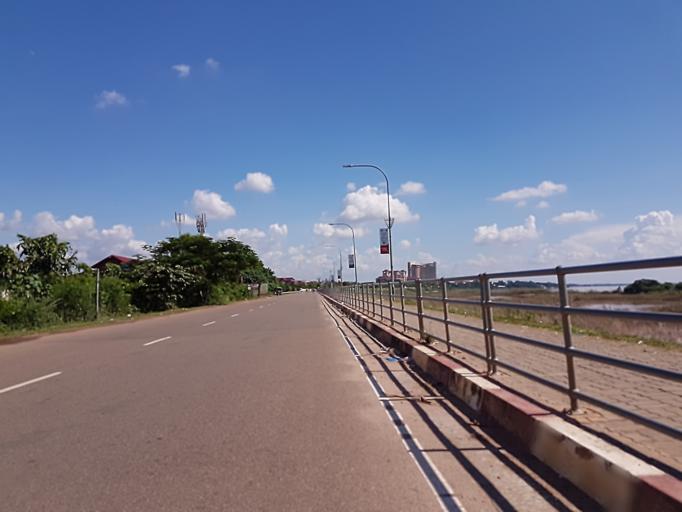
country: LA
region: Vientiane
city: Vientiane
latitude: 17.9550
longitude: 102.6127
